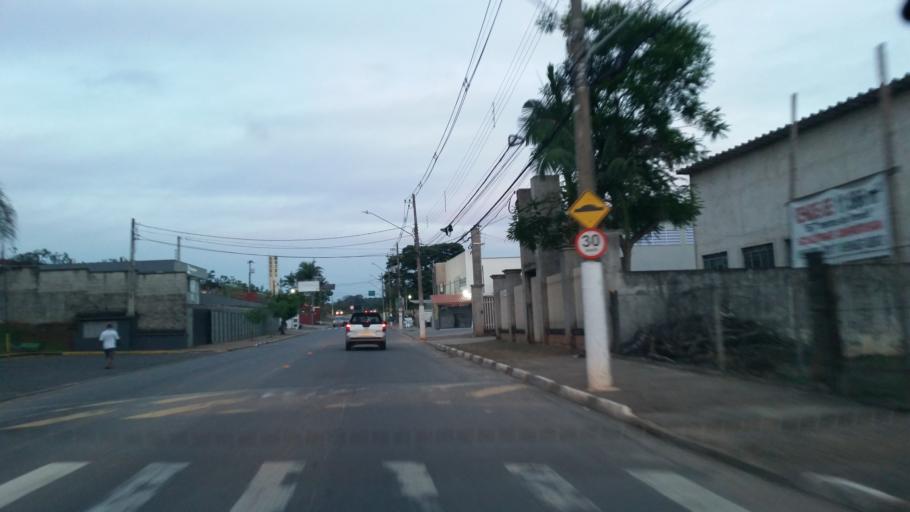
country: BR
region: Sao Paulo
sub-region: Atibaia
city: Atibaia
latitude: -23.1004
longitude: -46.5519
